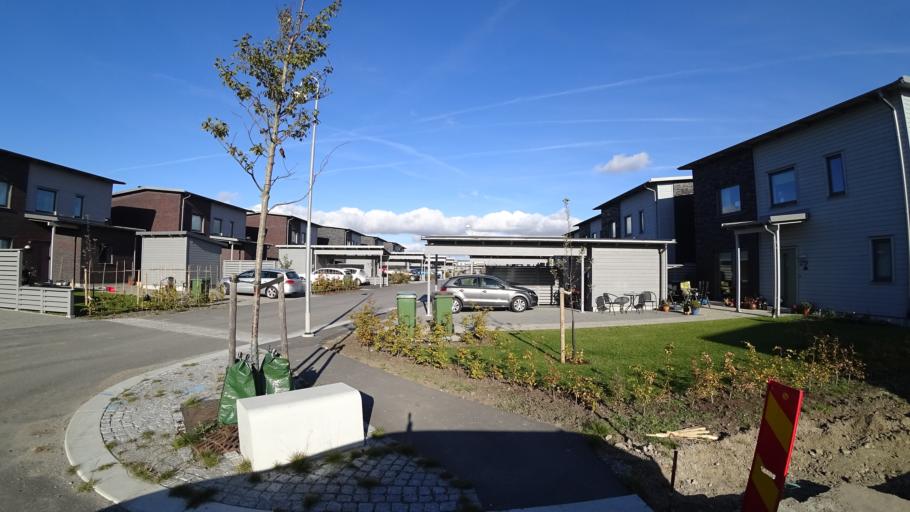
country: SE
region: Skane
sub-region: Staffanstorps Kommun
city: Hjaerup
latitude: 55.6710
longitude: 13.1531
